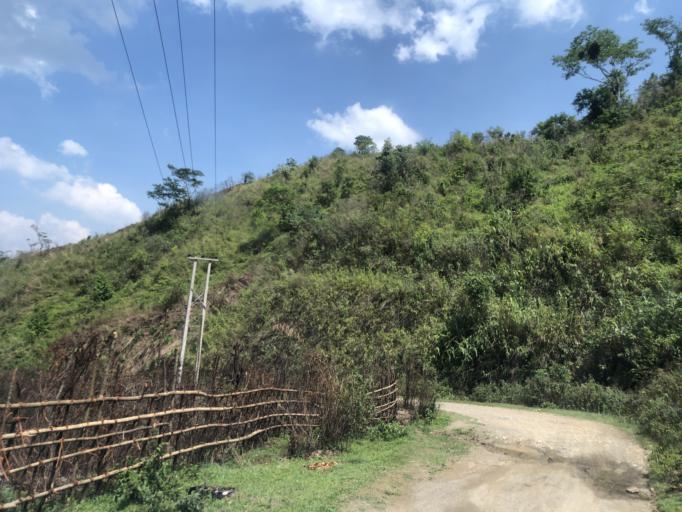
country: LA
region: Phongsali
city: Phongsali
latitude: 21.3965
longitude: 102.2173
